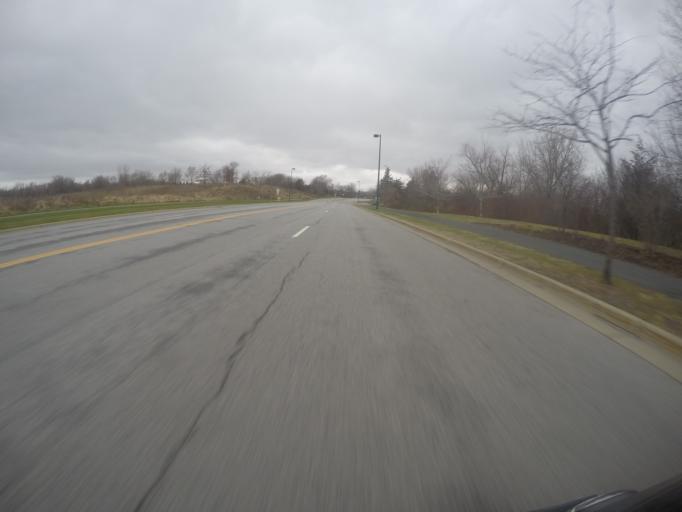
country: US
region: Minnesota
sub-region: Hennepin County
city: Eden Prairie
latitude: 44.8580
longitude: -93.4563
